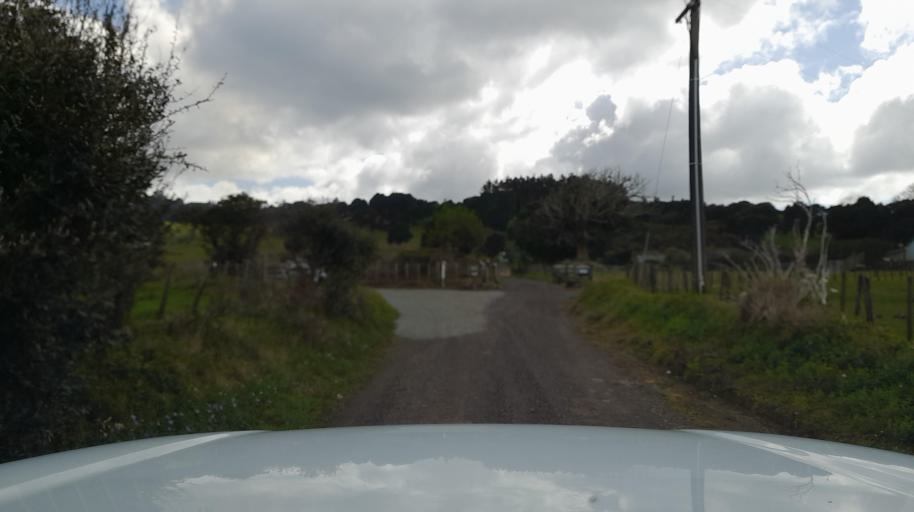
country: NZ
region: Northland
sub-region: Far North District
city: Waimate North
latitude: -35.3734
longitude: 173.8592
